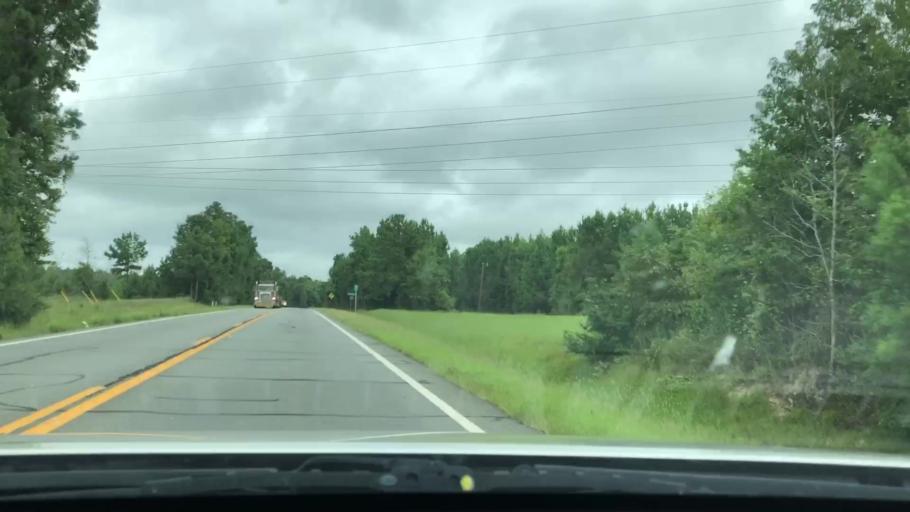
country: US
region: Georgia
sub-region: Pike County
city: Zebulon
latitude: 33.0445
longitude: -84.4900
